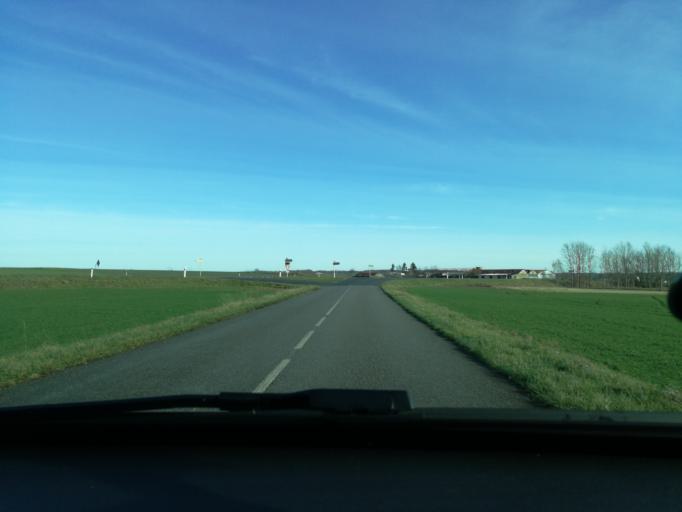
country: FR
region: Lorraine
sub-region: Departement de la Meuse
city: Fains-Veel
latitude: 48.8159
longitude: 5.1004
